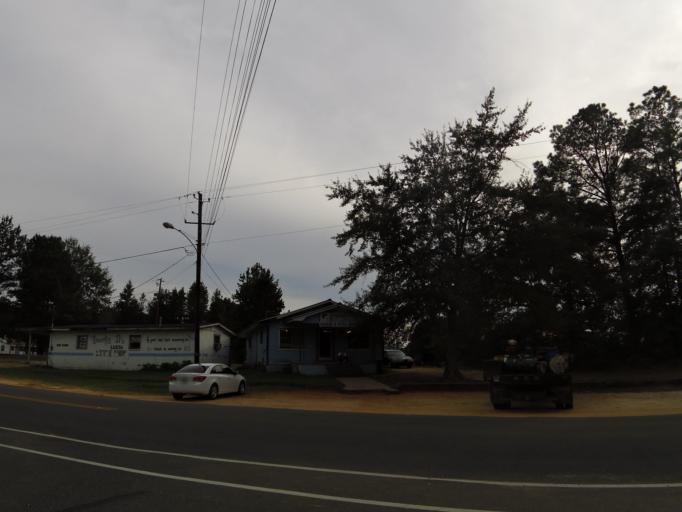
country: US
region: Alabama
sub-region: Monroe County
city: Monroeville
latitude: 31.5282
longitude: -87.3425
